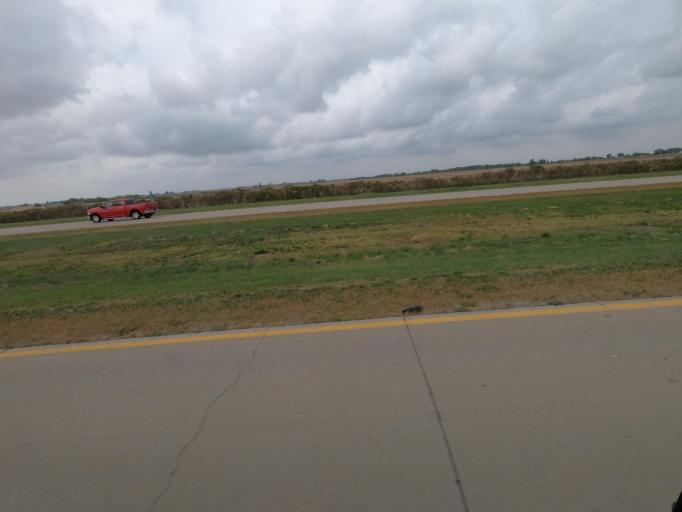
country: US
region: Iowa
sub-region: Wapello County
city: Ottumwa
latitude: 41.0019
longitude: -92.2577
